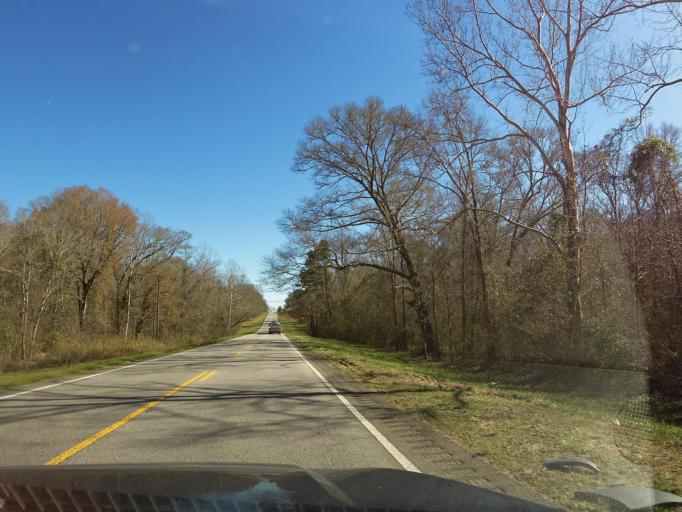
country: US
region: Alabama
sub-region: Bullock County
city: Union Springs
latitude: 32.0838
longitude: -85.5378
